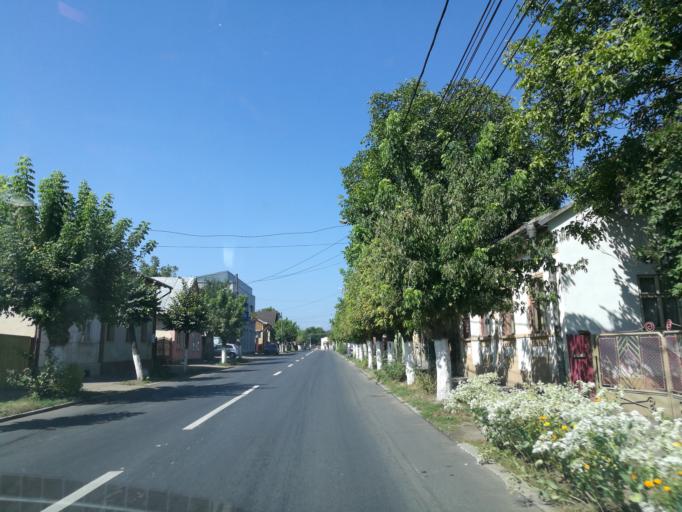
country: RO
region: Suceava
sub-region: Municipiul Suceava
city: Radauti
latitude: 47.8465
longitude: 25.9071
